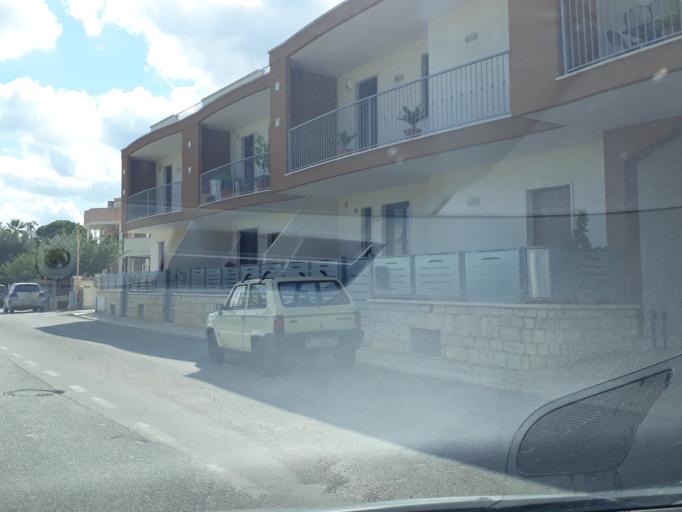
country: IT
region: Apulia
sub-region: Provincia di Brindisi
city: Fasano
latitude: 40.8290
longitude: 17.3669
